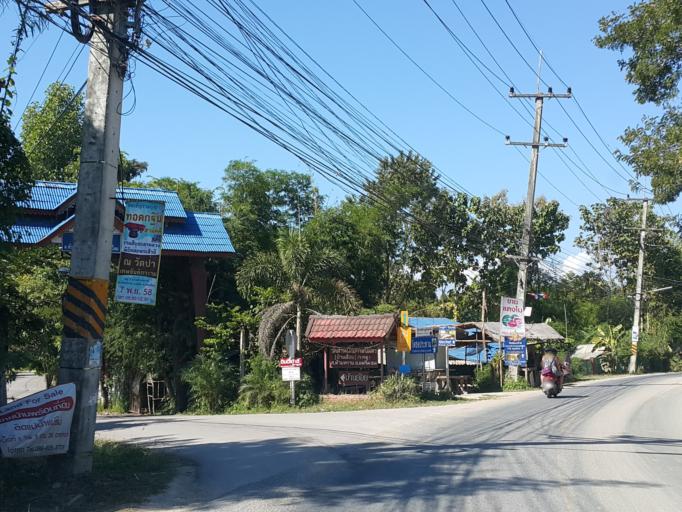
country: TH
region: Chiang Mai
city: San Sai
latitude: 18.9409
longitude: 98.9297
